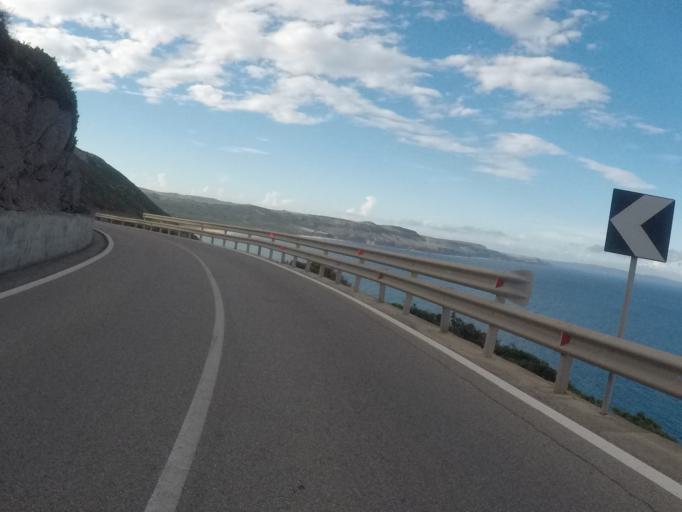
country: IT
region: Sardinia
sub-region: Provincia di Carbonia-Iglesias
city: Gonnesa
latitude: 39.3061
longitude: 8.4354
